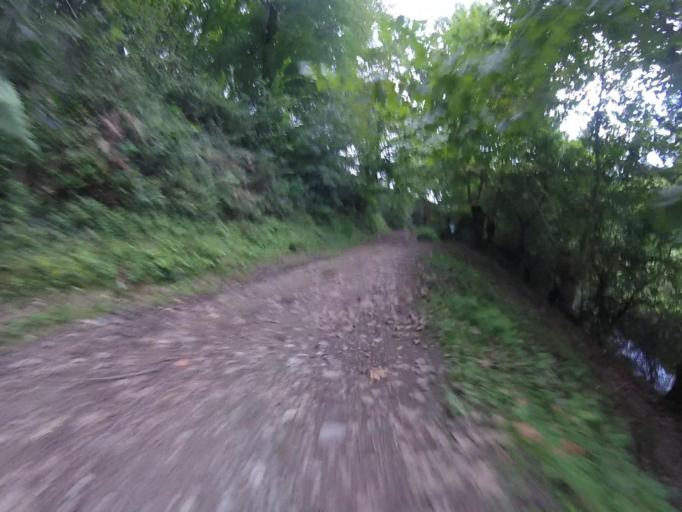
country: ES
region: Basque Country
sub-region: Provincia de Guipuzcoa
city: Errenteria
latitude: 43.2768
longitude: -1.8472
